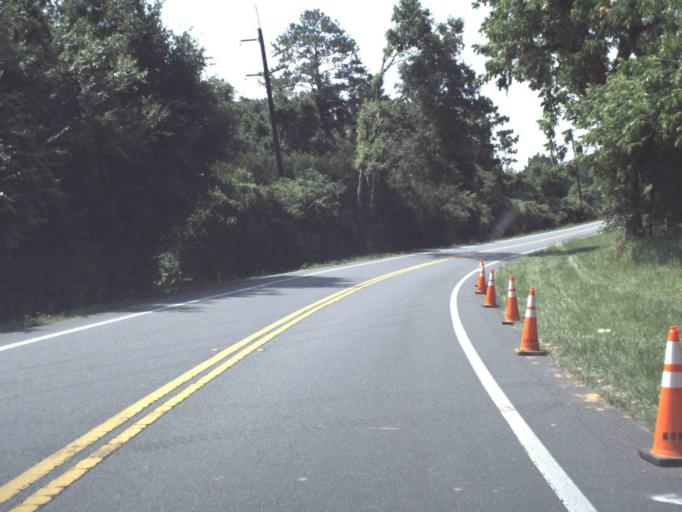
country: US
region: Florida
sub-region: Clay County
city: Keystone Heights
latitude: 29.6841
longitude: -82.0355
